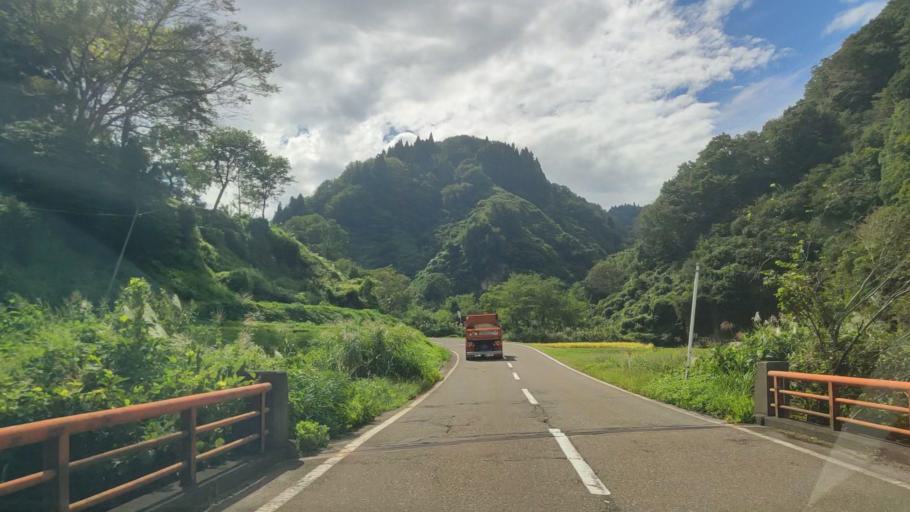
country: JP
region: Niigata
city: Arai
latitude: 36.9413
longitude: 138.2915
